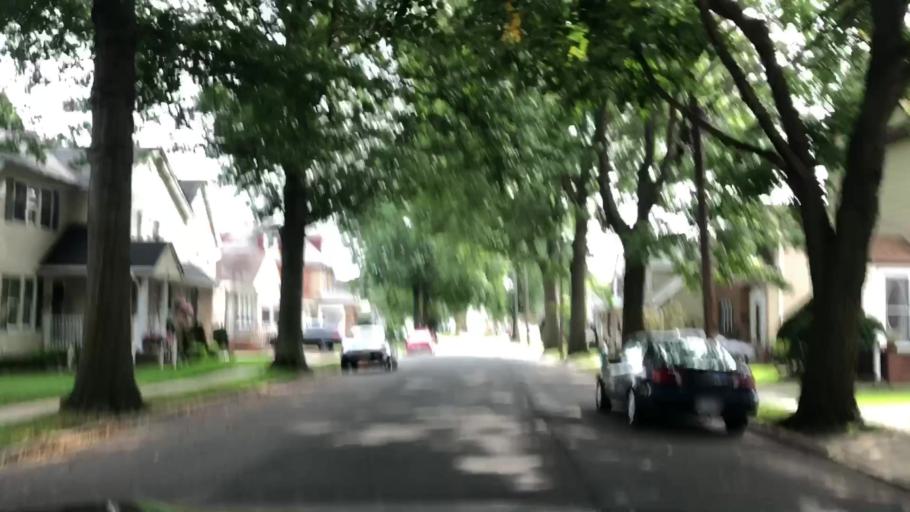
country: US
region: New York
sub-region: Nassau County
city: Floral Park
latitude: 40.7285
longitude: -73.6974
